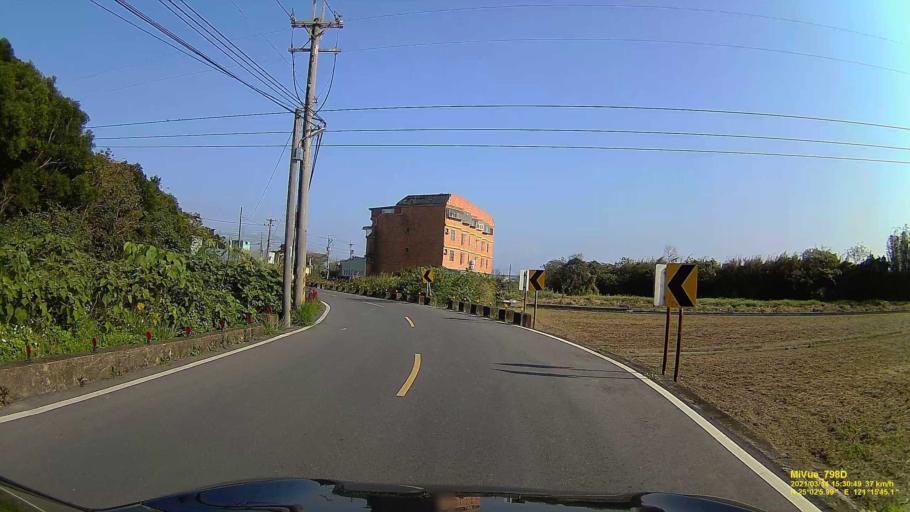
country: TW
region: Taiwan
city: Taoyuan City
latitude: 25.0348
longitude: 121.2627
